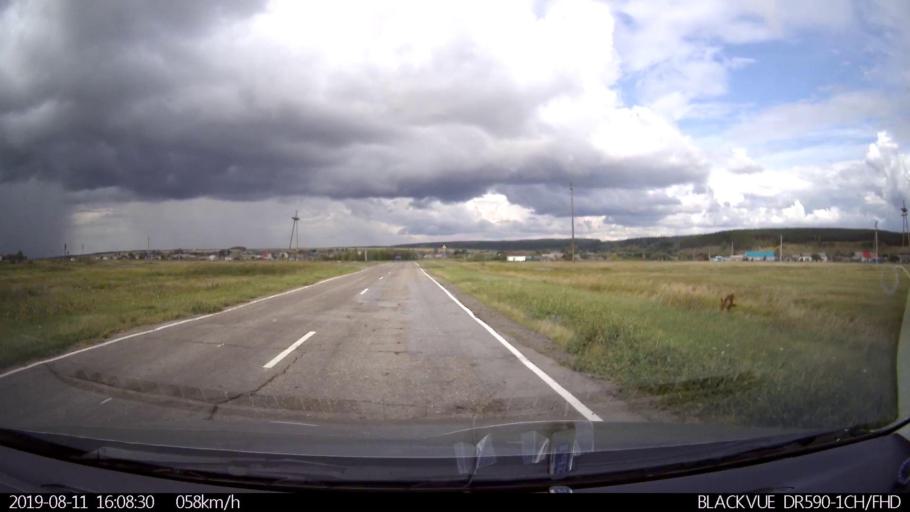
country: RU
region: Ulyanovsk
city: Ignatovka
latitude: 53.9852
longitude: 47.6482
